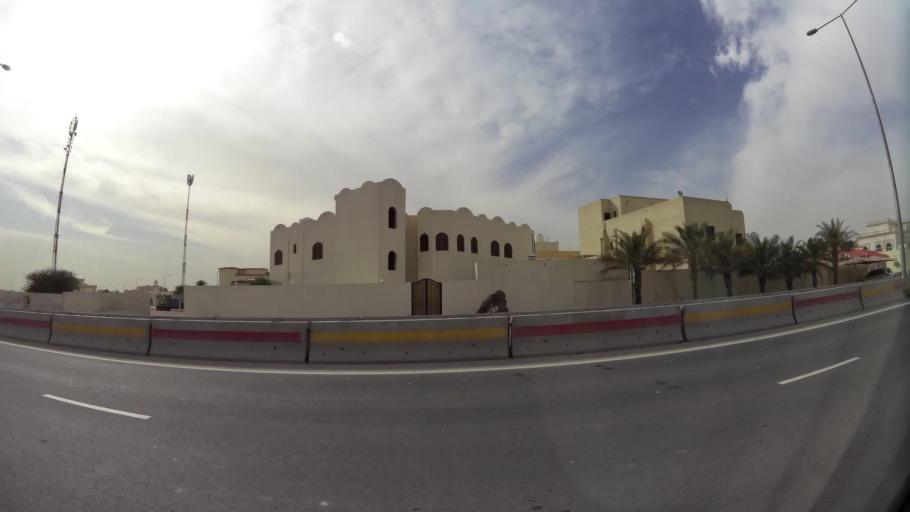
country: QA
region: Baladiyat ar Rayyan
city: Ar Rayyan
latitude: 25.3135
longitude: 51.4161
